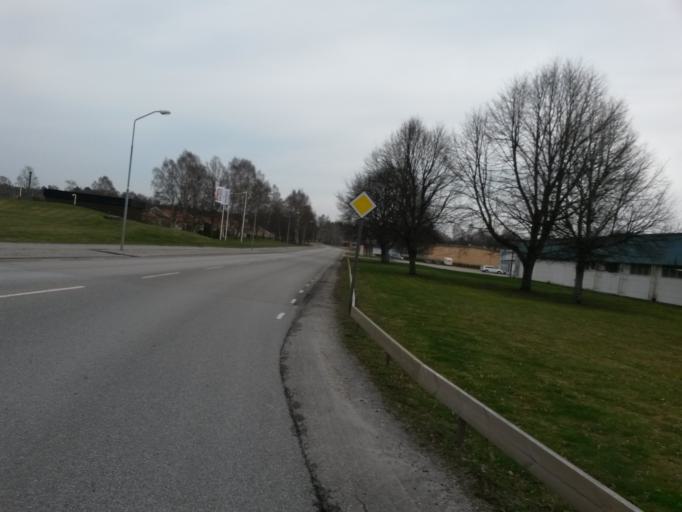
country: SE
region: Vaestra Goetaland
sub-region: Herrljunga Kommun
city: Herrljunga
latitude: 58.0743
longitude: 13.0202
